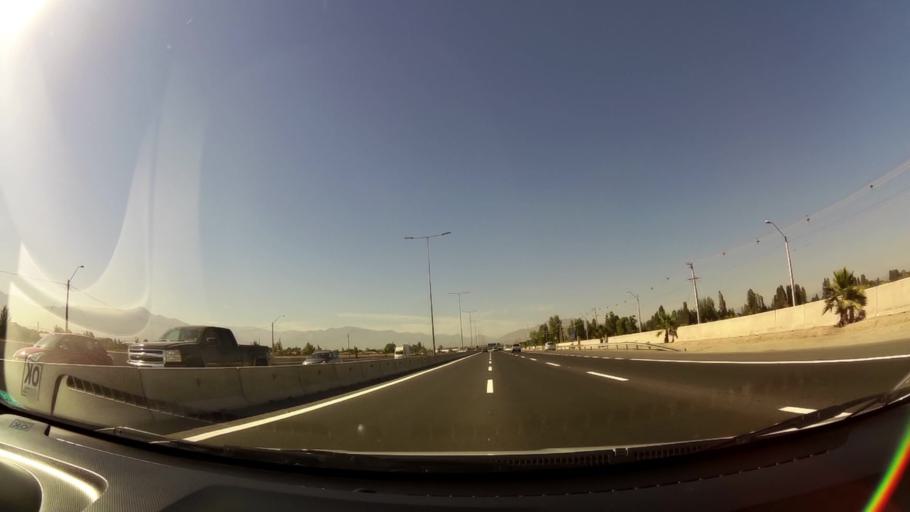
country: CL
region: Santiago Metropolitan
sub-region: Provincia de Santiago
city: La Pintana
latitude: -33.5763
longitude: -70.6118
